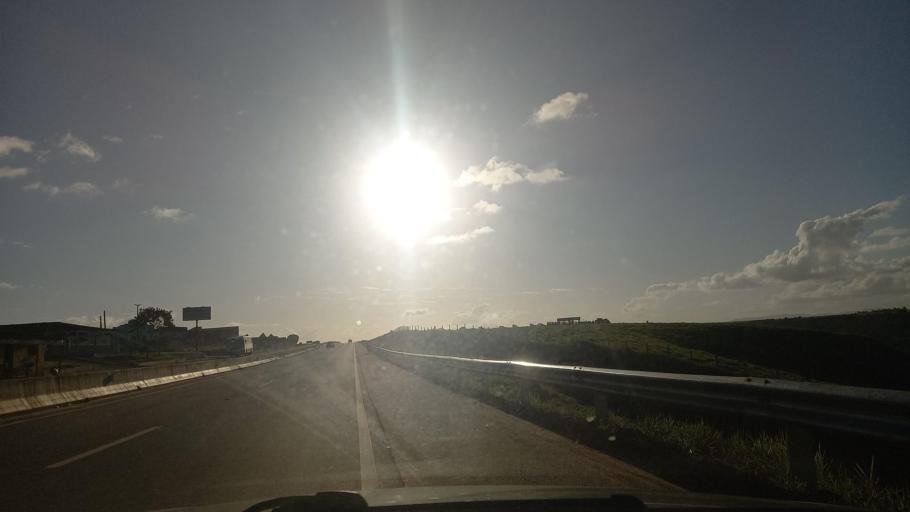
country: BR
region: Alagoas
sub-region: Campo Alegre
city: Campo Alegre
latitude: -9.8024
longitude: -36.2748
